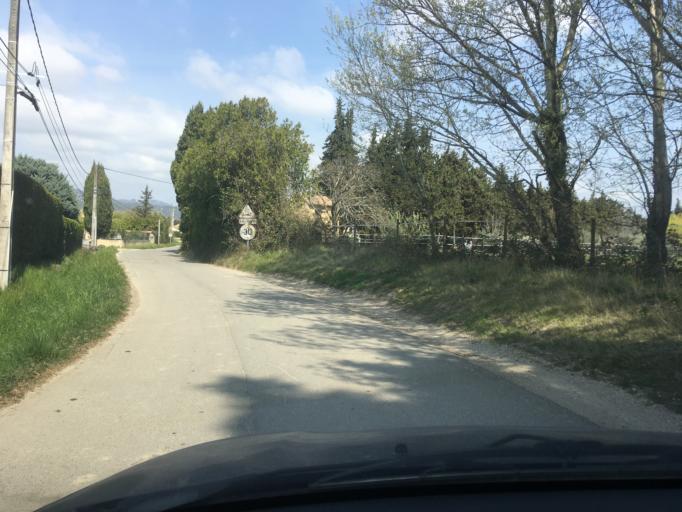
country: FR
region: Provence-Alpes-Cote d'Azur
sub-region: Departement du Vaucluse
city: Aubignan
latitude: 44.0919
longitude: 5.0179
